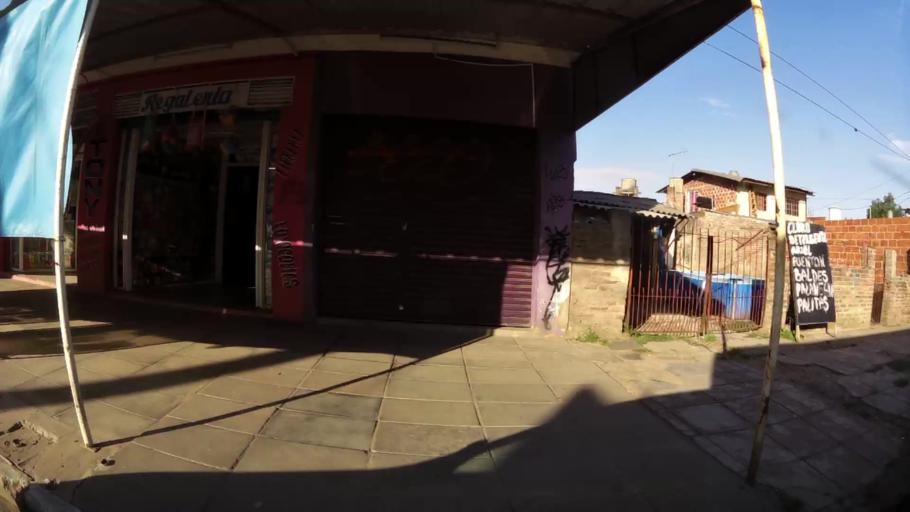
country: AR
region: Buenos Aires
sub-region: Partido de Merlo
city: Merlo
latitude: -34.6905
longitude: -58.7486
